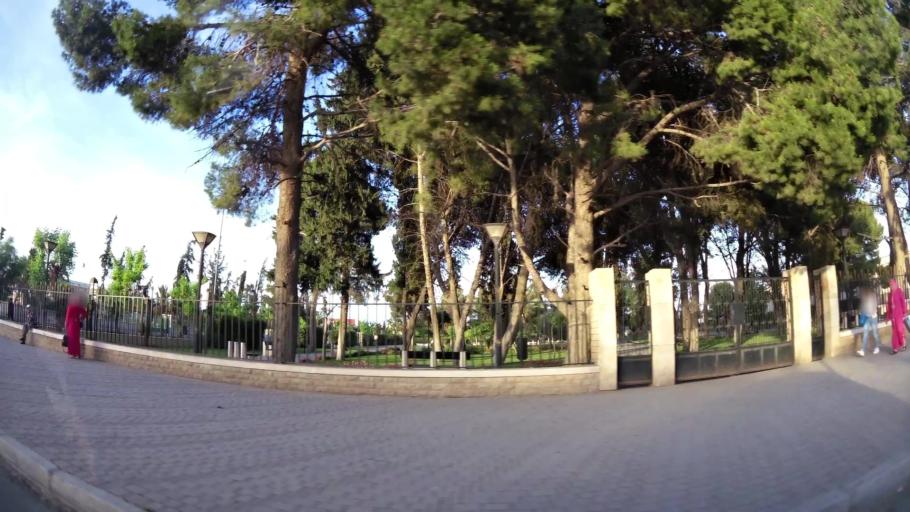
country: MA
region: Oriental
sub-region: Oujda-Angad
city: Oujda
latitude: 34.6804
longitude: -1.8896
